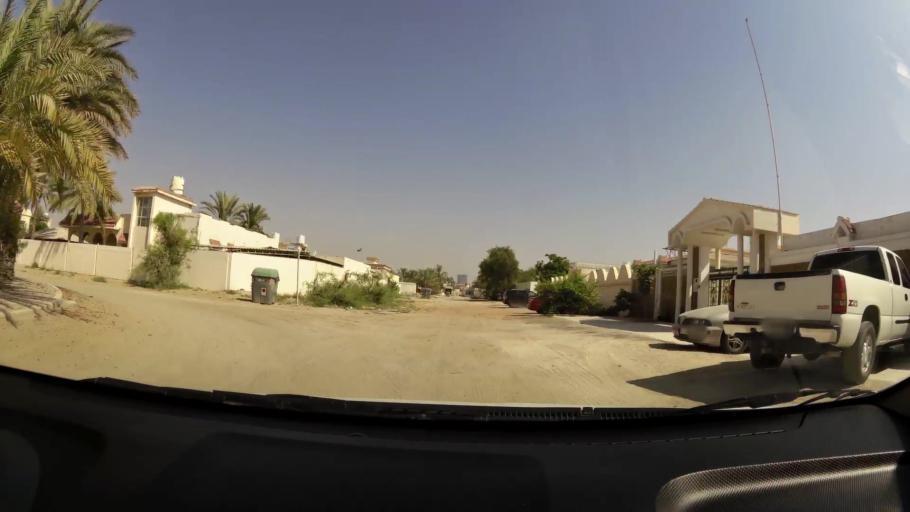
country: AE
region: Ajman
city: Ajman
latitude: 25.4177
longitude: 55.4663
